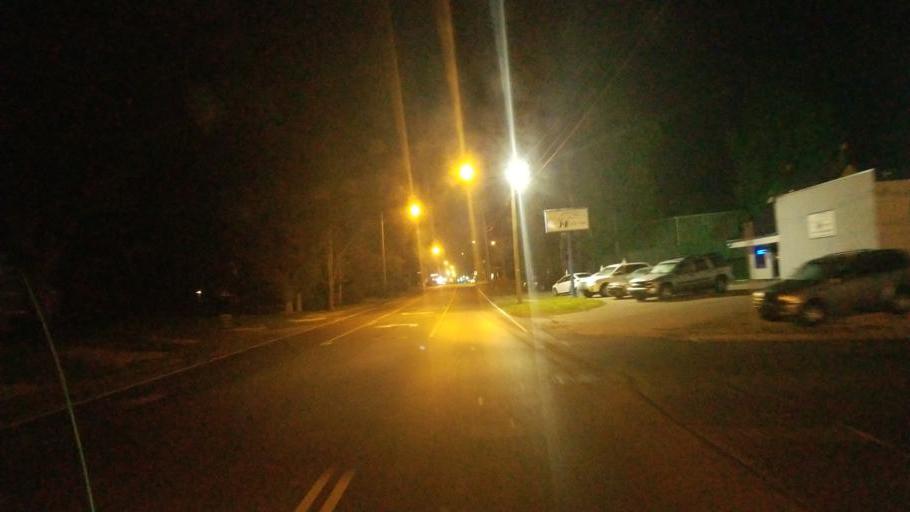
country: US
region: Ohio
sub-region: Licking County
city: Newark
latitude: 40.0798
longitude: -82.4162
